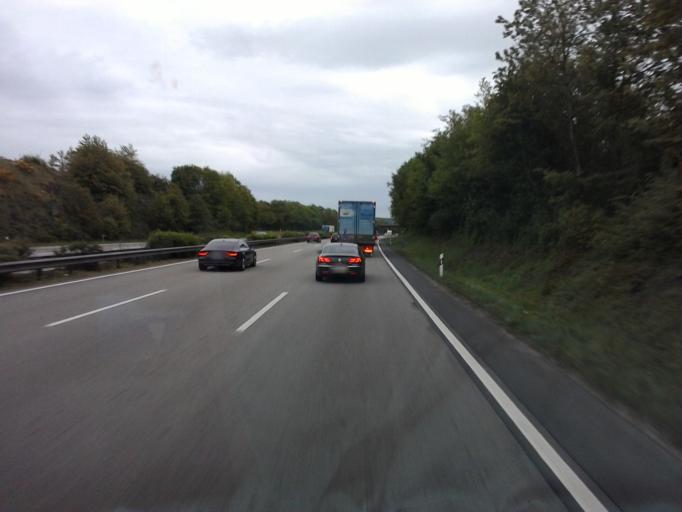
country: DE
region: Rheinland-Pfalz
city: Niederzissen
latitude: 50.4710
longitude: 7.2295
